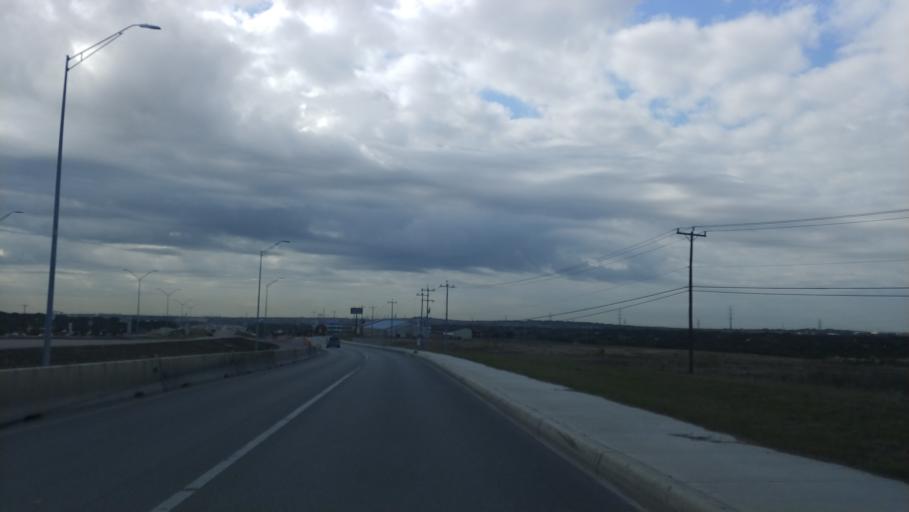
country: US
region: Texas
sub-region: Bexar County
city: Leon Valley
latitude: 29.4536
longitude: -98.7116
